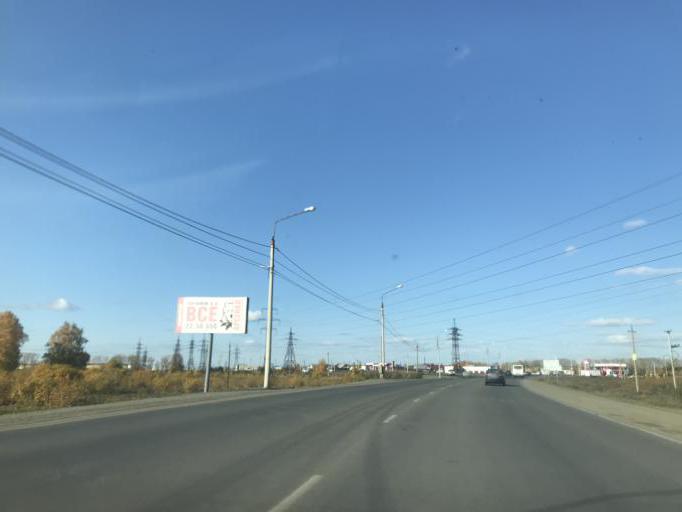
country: RU
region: Chelyabinsk
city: Roshchino
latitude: 55.2272
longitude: 61.2876
